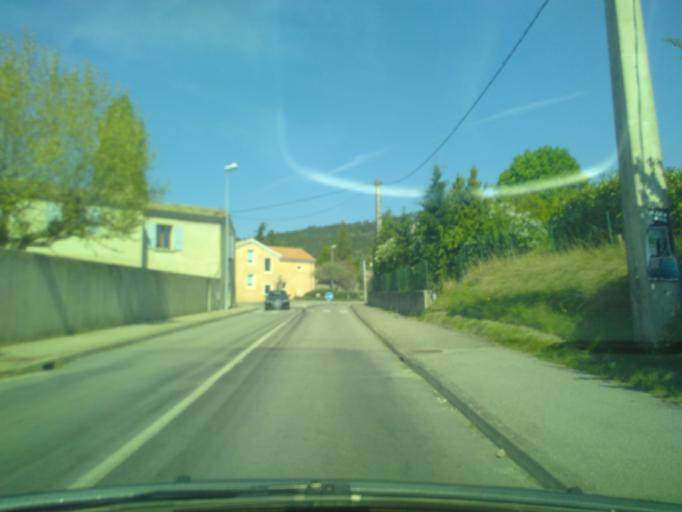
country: FR
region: Rhone-Alpes
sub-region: Departement de la Drome
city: La Begude-de-Mazenc
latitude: 44.6269
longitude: 4.9699
